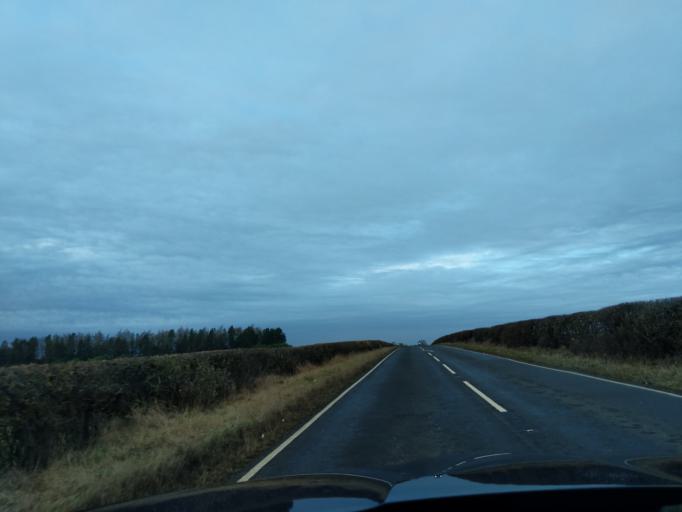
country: GB
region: England
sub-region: Northumberland
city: Hartburn
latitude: 55.1154
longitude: -1.8964
